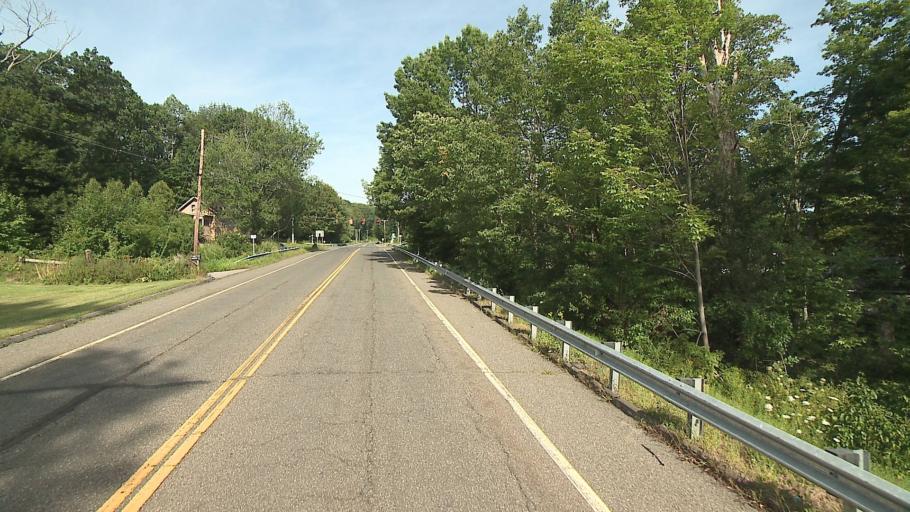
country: US
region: Connecticut
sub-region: Litchfield County
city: Thomaston
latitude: 41.6970
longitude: -73.1055
